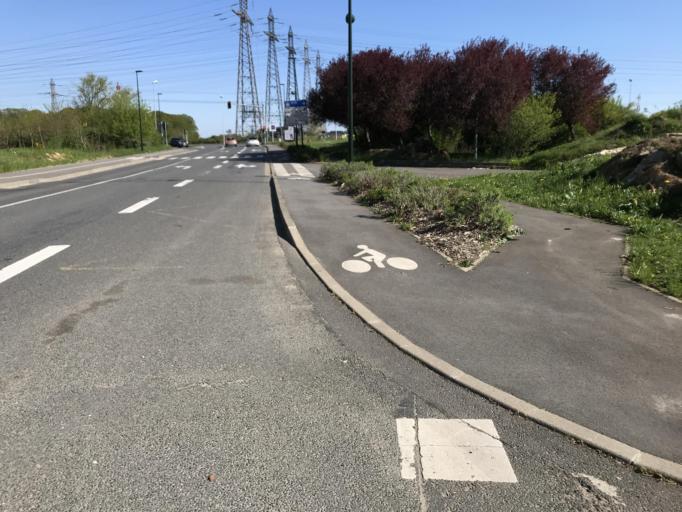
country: FR
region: Ile-de-France
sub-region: Departement de l'Essonne
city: Villejust
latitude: 48.6897
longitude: 2.2289
